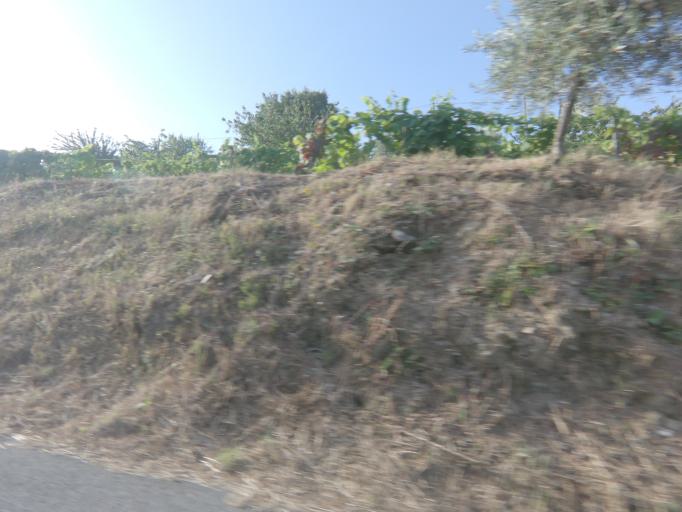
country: PT
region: Vila Real
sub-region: Sabrosa
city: Sabrosa
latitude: 41.2246
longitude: -7.5060
